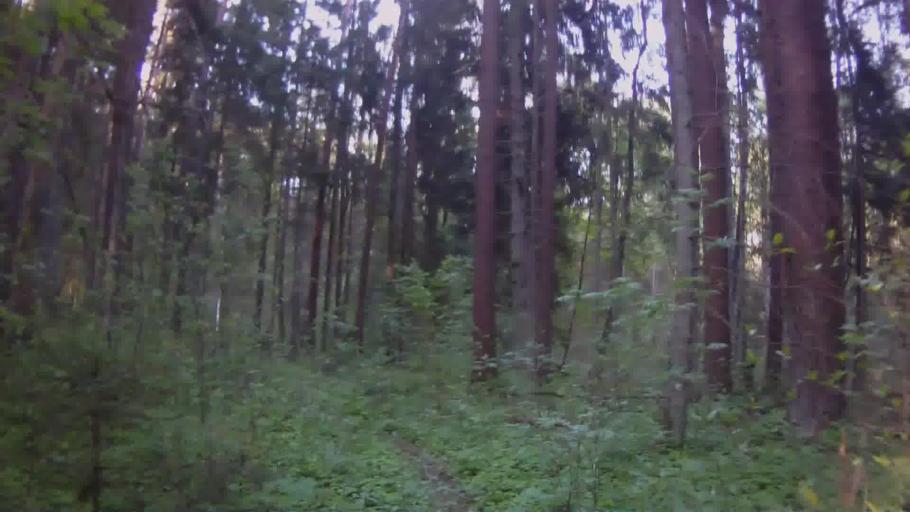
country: LV
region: Baldone
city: Baldone
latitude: 56.7480
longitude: 24.4209
